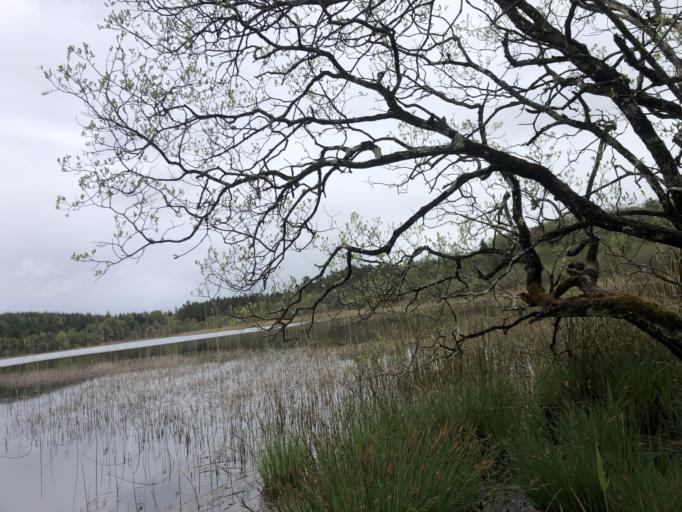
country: IE
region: Connaught
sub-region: County Leitrim
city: Carrick-on-Shannon
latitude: 53.9878
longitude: -8.1866
